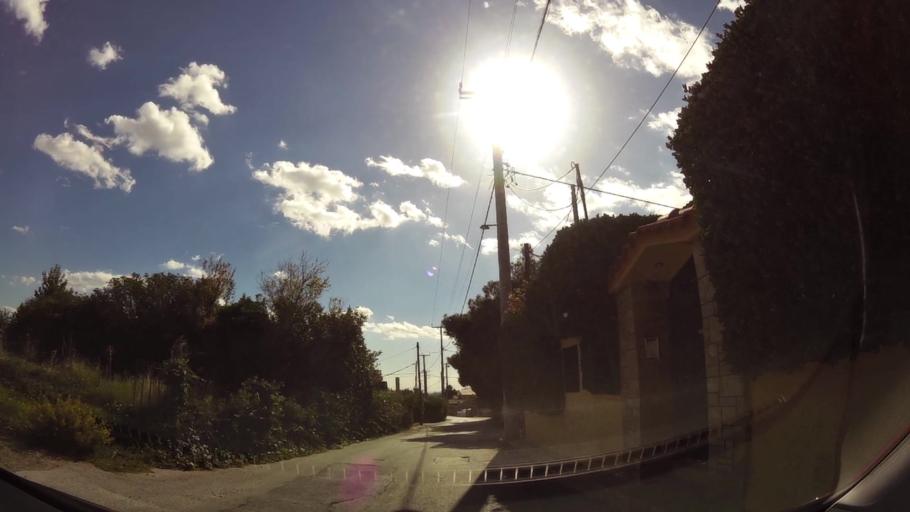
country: GR
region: Attica
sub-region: Nomarchia Anatolikis Attikis
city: Thrakomakedones
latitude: 38.1196
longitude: 23.7307
